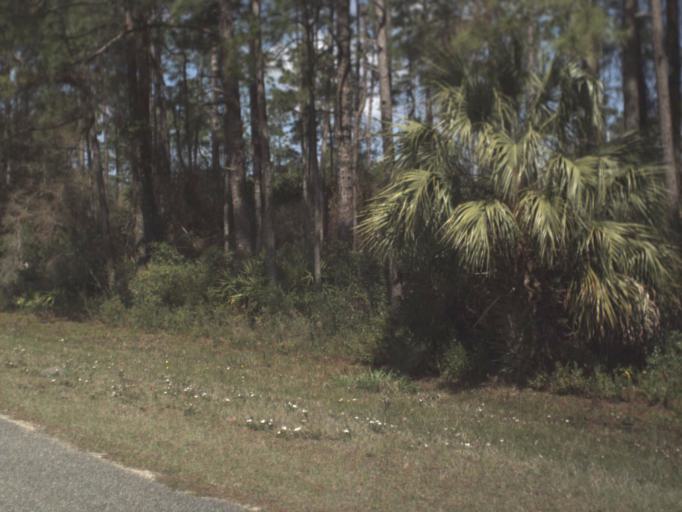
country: US
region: Florida
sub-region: Franklin County
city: Apalachicola
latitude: 29.7340
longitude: -85.1503
